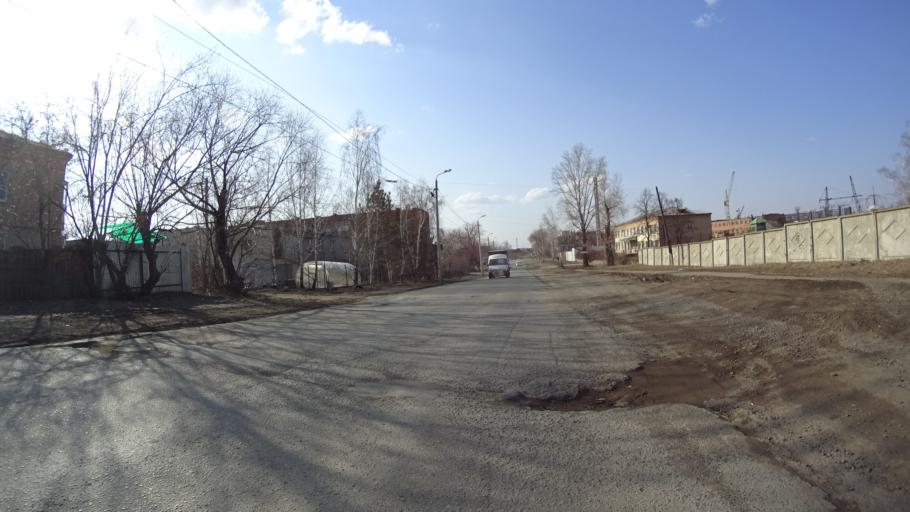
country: RU
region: Chelyabinsk
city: Novosineglazovskiy
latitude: 55.1057
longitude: 61.3389
